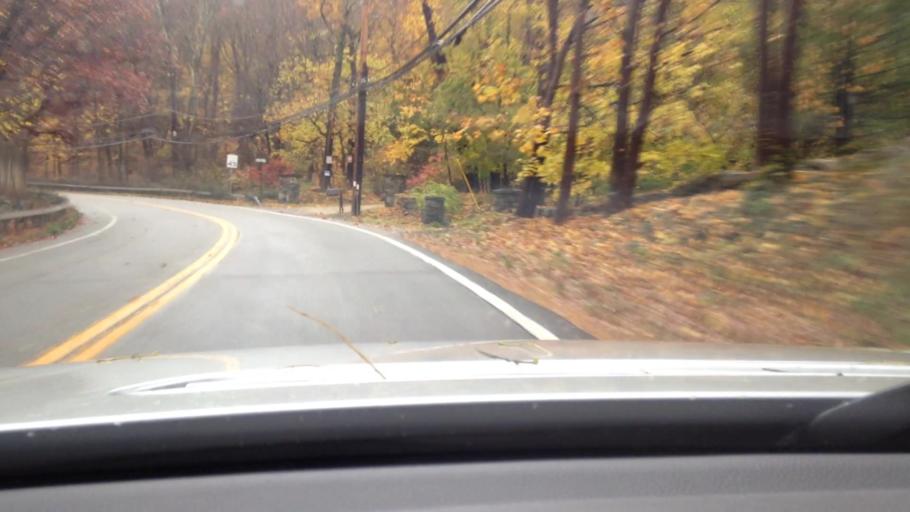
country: US
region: New York
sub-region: Orange County
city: West Point
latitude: 41.3739
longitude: -73.9396
